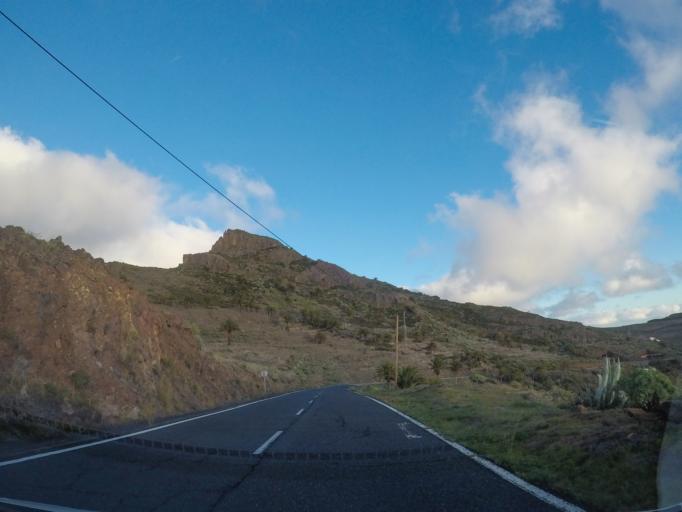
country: ES
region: Canary Islands
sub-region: Provincia de Santa Cruz de Tenerife
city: Alajero
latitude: 28.0758
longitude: -17.2406
